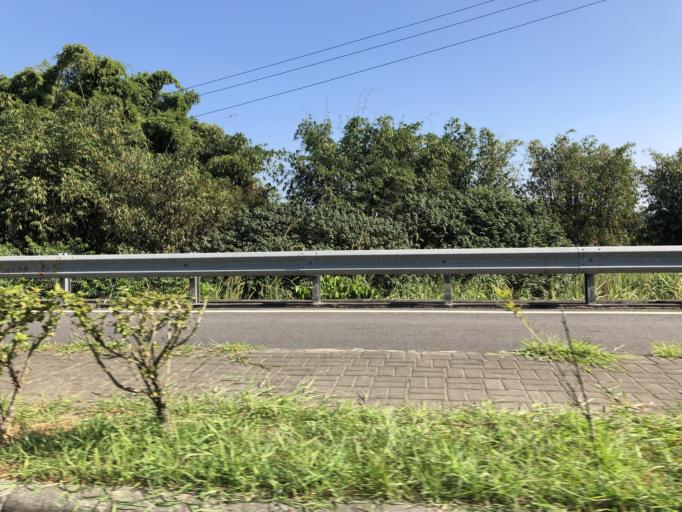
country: TW
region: Taiwan
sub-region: Tainan
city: Tainan
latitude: 23.0321
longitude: 120.3225
